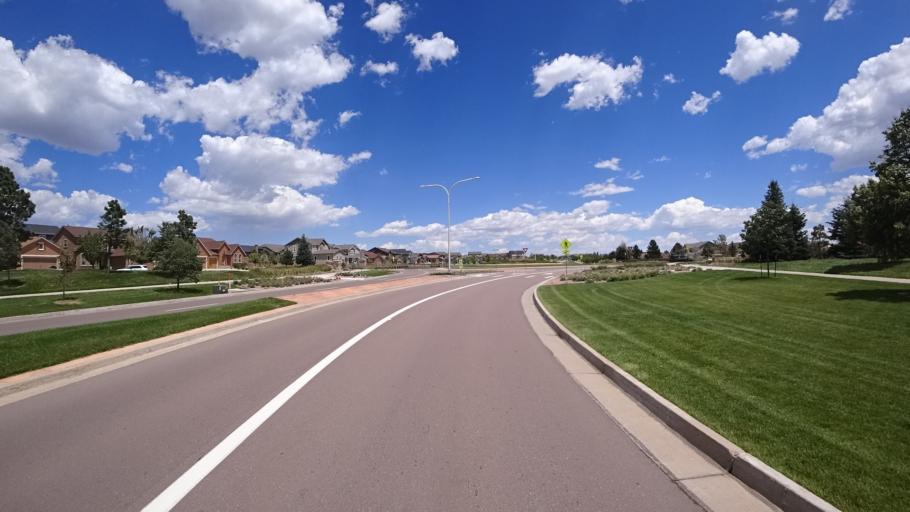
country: US
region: Colorado
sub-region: El Paso County
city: Black Forest
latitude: 38.9605
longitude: -104.7186
